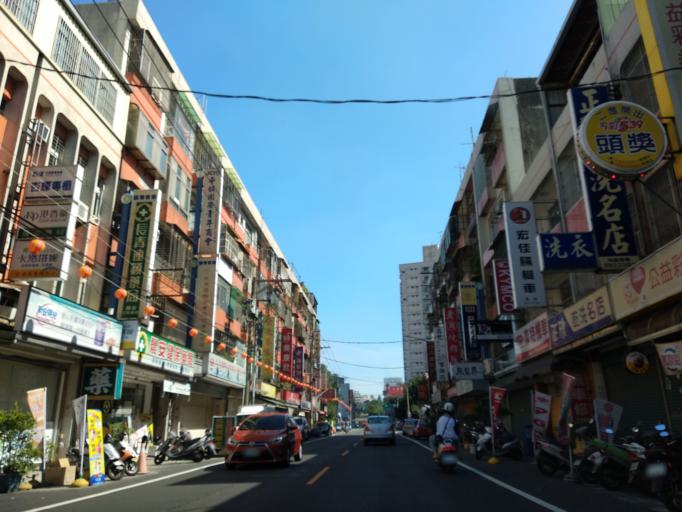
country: TW
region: Taiwan
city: Taoyuan City
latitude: 24.9462
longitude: 121.2139
